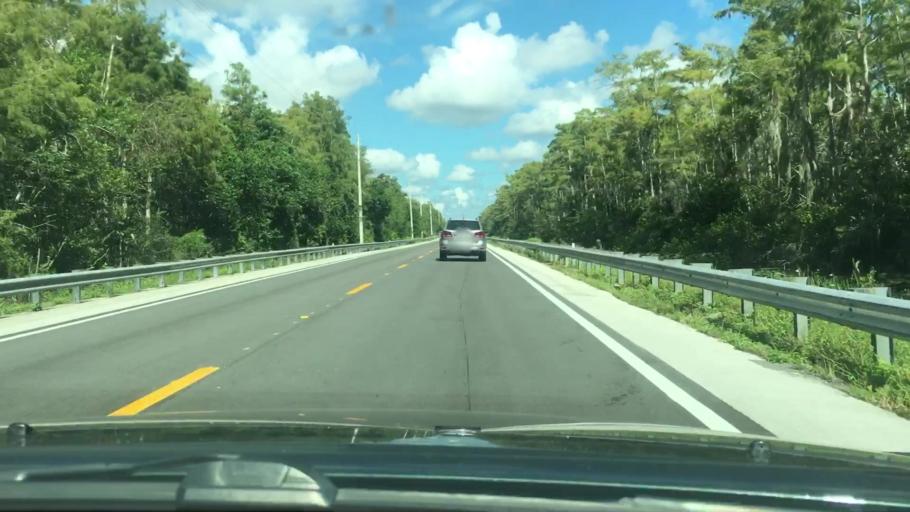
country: US
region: Florida
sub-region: Miami-Dade County
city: Kendall West
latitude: 25.8003
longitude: -80.8677
